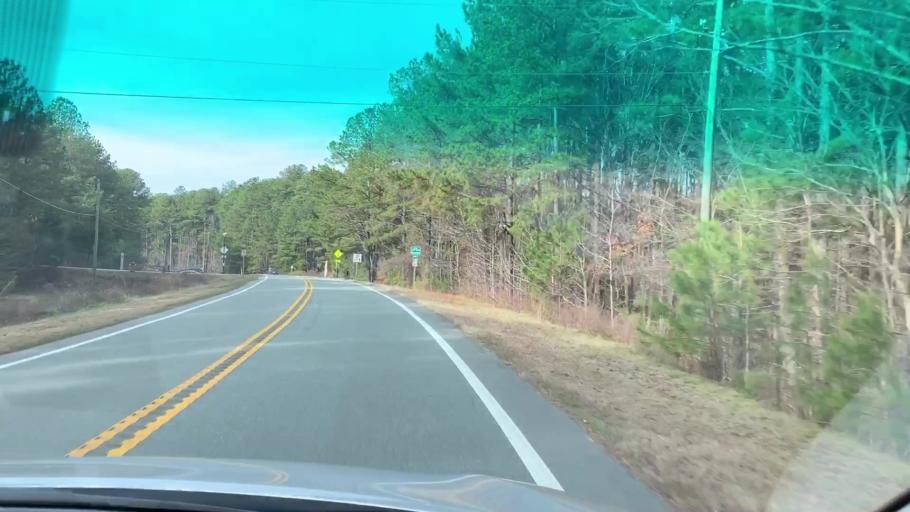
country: US
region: North Carolina
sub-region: Wake County
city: Green Level
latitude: 35.8469
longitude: -78.9248
